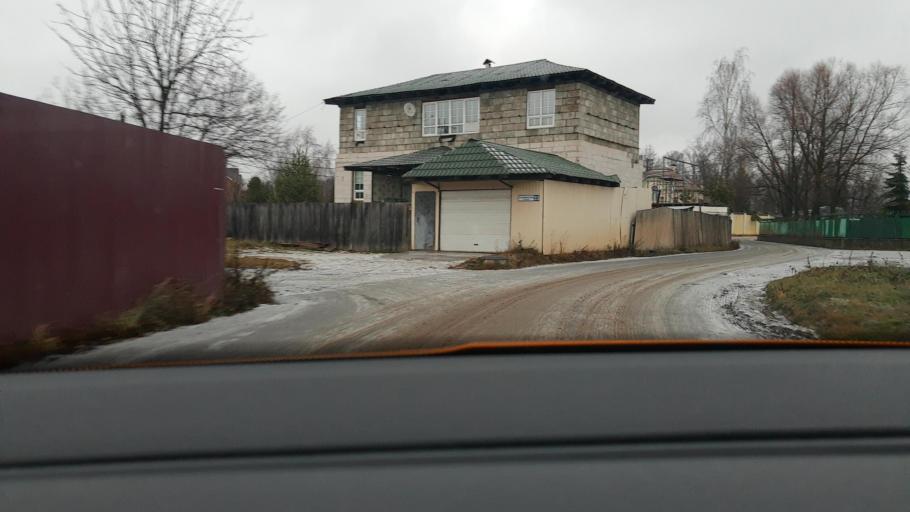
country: RU
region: Moscow
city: Severnyy
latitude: 55.9565
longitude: 37.5584
